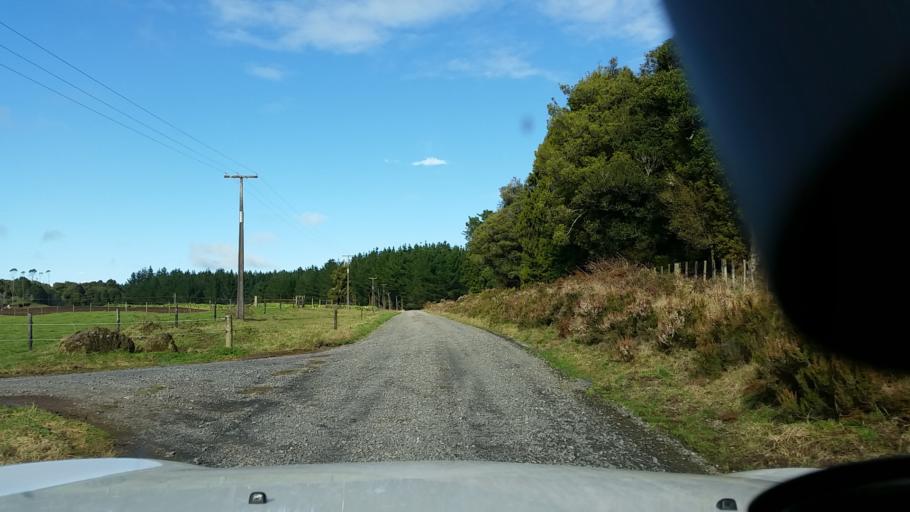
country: NZ
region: Bay of Plenty
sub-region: Rotorua District
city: Rotorua
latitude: -38.0791
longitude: 176.0398
